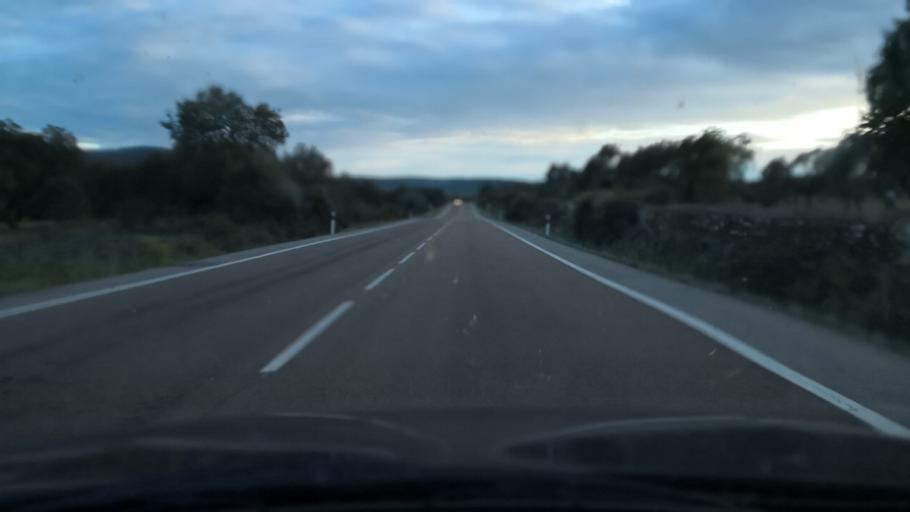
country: ES
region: Extremadura
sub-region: Provincia de Badajoz
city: Puebla de Obando
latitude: 39.2287
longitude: -6.5707
